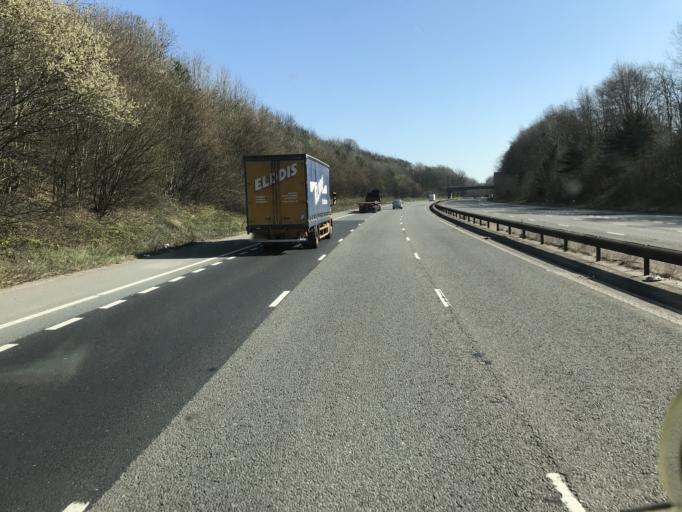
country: GB
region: England
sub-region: Borough of Halton
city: Halton
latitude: 53.3129
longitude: -2.6983
